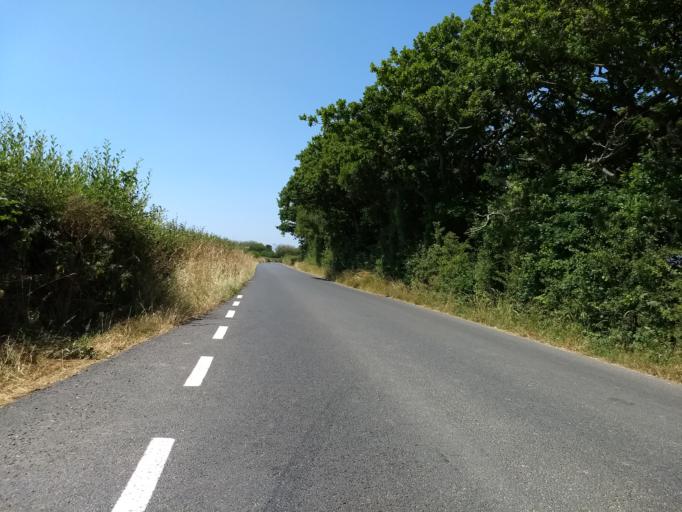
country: GB
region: England
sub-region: Isle of Wight
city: Northwood
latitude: 50.7093
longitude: -1.3521
